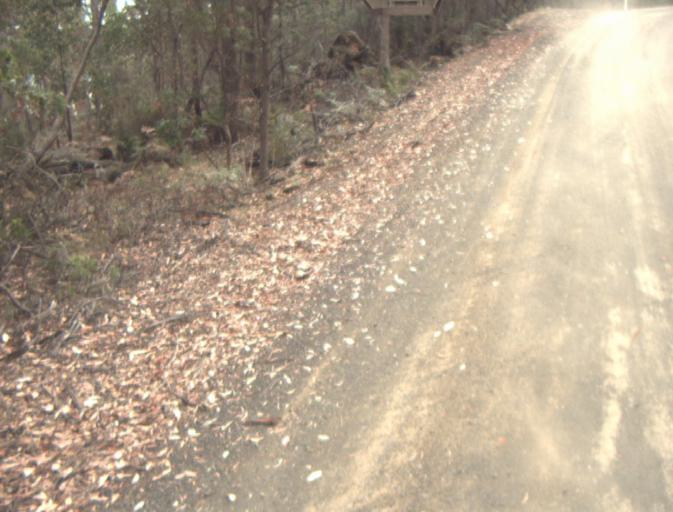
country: AU
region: Tasmania
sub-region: Northern Midlands
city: Evandale
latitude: -41.4941
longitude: 147.5531
